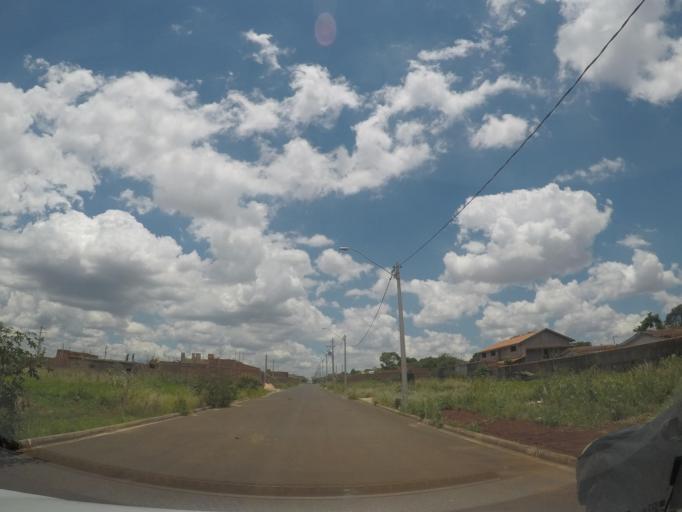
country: BR
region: Sao Paulo
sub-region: Hortolandia
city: Hortolandia
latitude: -22.8397
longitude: -47.2307
